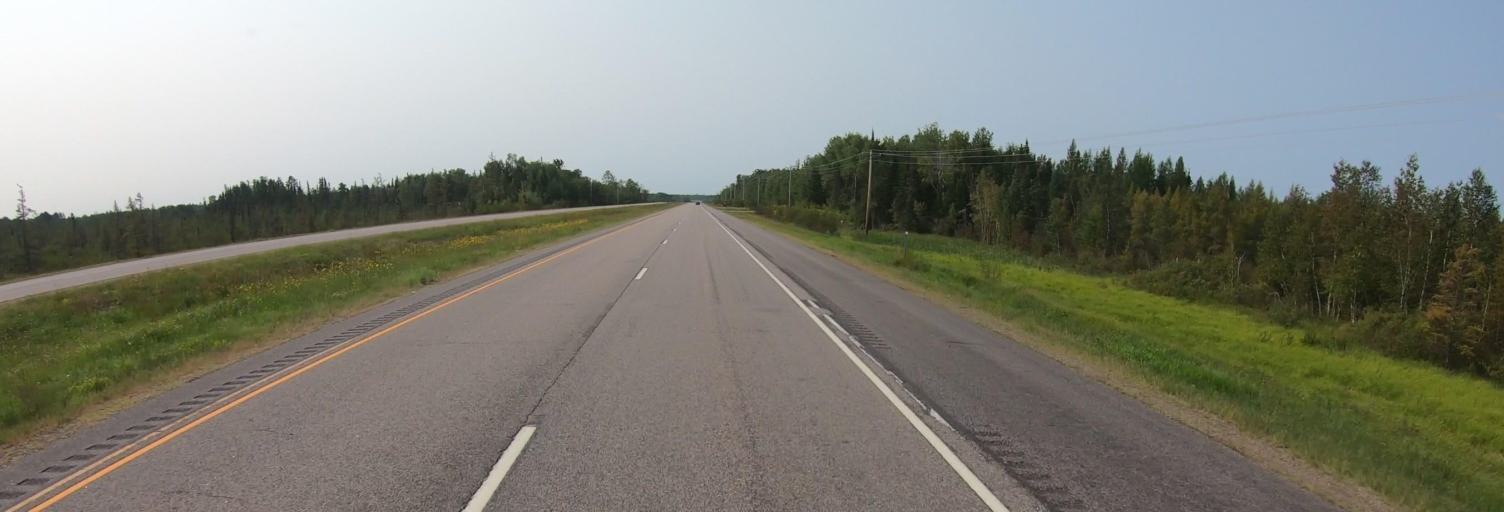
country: US
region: Minnesota
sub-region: Saint Louis County
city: Parkville
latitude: 47.6215
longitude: -92.5540
